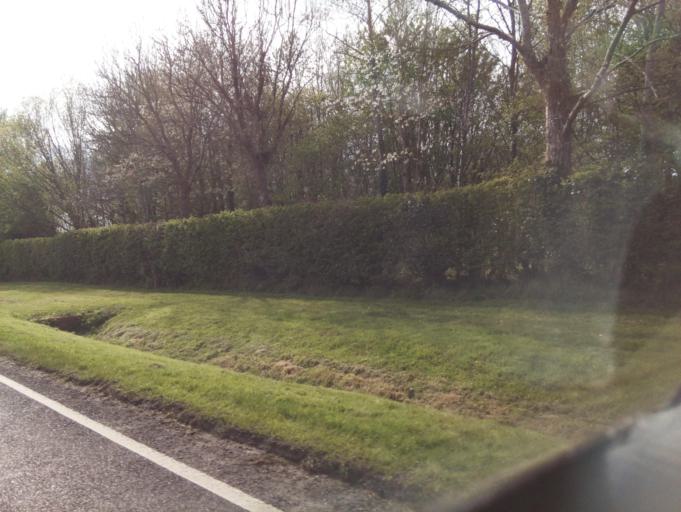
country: GB
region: England
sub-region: Hampshire
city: Chandlers Ford
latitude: 51.0088
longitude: -1.4077
